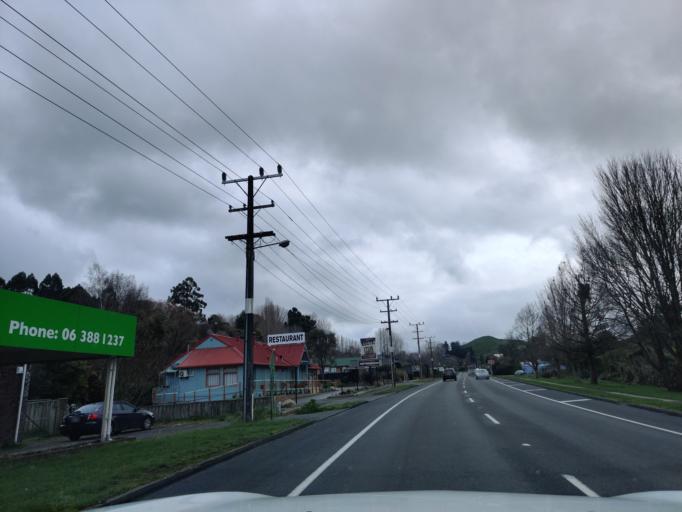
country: NZ
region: Manawatu-Wanganui
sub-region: Ruapehu District
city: Waiouru
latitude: -39.6738
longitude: 175.7934
